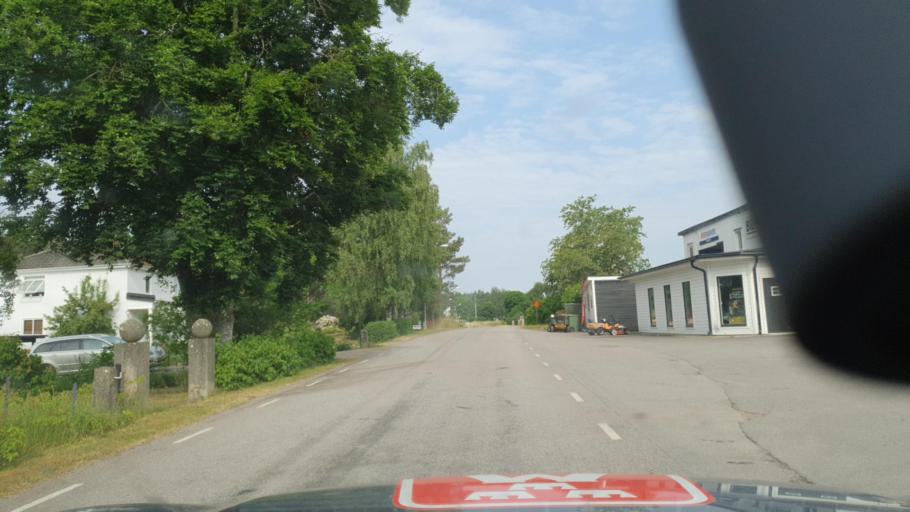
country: SE
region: Kalmar
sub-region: Kalmar Kommun
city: Trekanten
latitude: 56.6168
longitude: 16.0544
